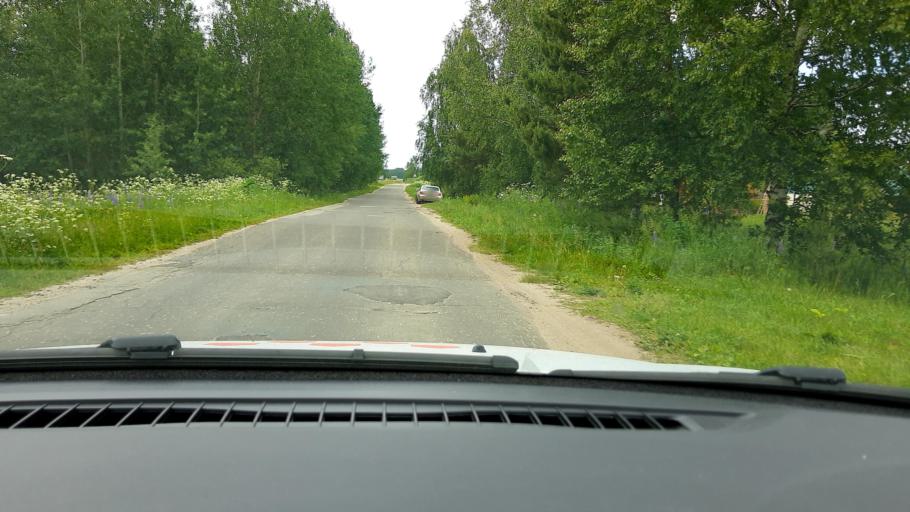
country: RU
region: Nizjnij Novgorod
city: Sitniki
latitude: 56.5237
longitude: 44.1065
